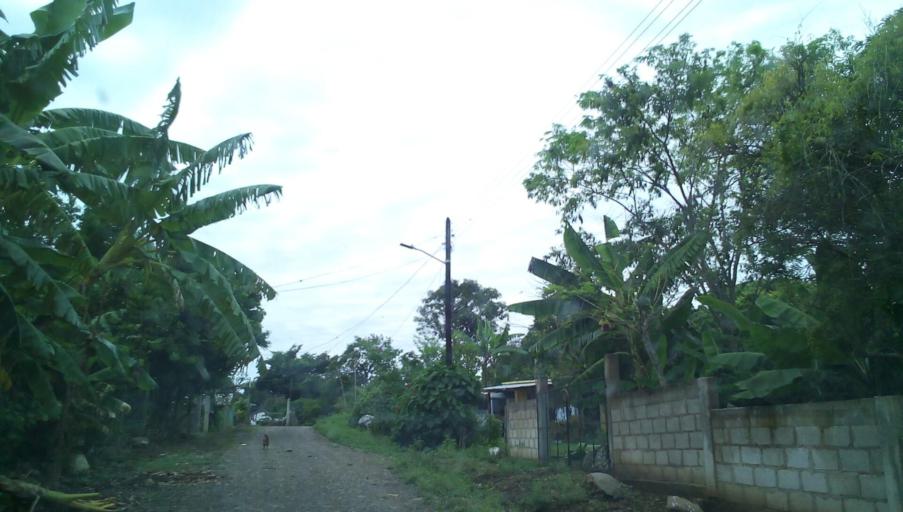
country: MX
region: Veracruz
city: Tepetzintla
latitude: 21.1284
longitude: -97.8579
